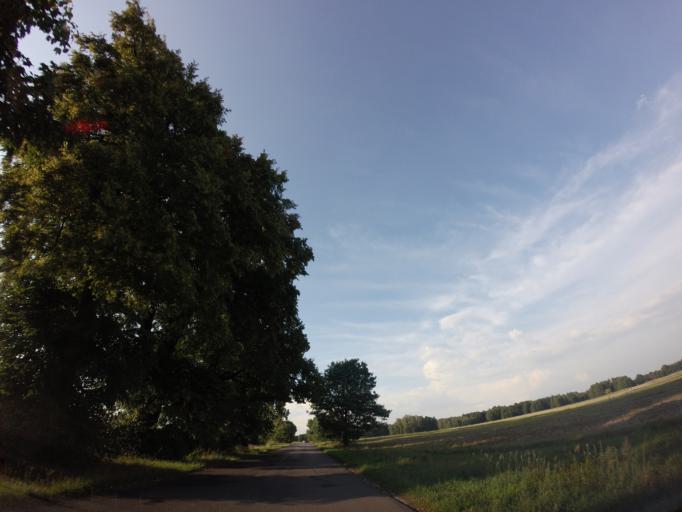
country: PL
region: Lublin Voivodeship
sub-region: Powiat pulawski
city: Kurow
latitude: 51.4180
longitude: 22.2017
